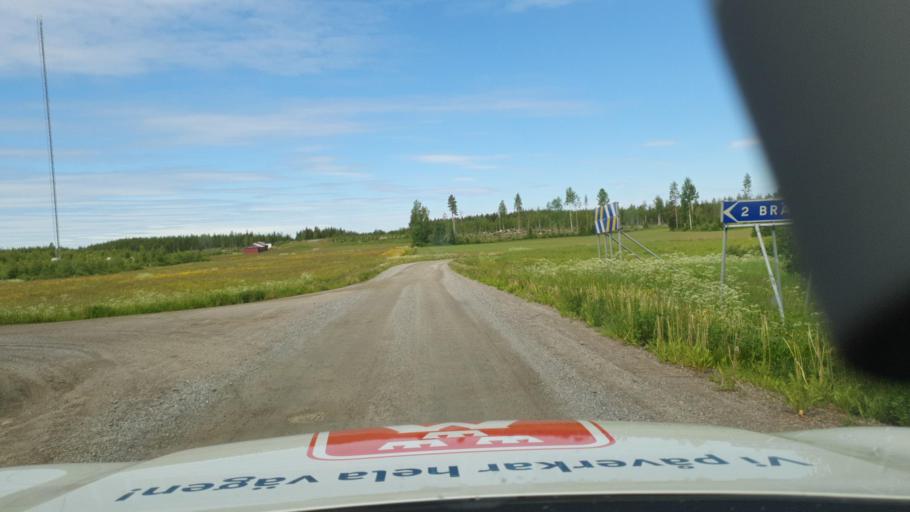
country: SE
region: Vaesterbotten
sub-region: Skelleftea Kommun
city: Forsbacka
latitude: 64.6784
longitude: 20.5212
